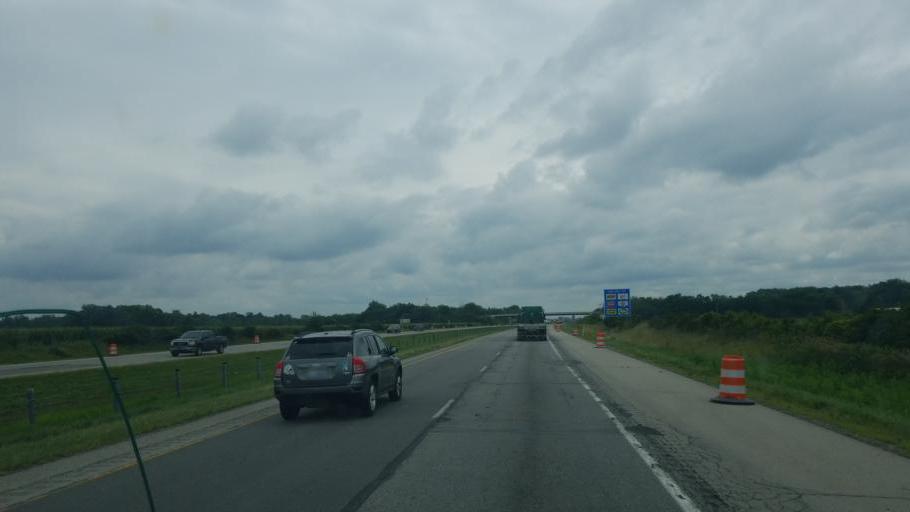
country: US
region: Indiana
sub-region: Madison County
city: Anderson
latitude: 40.0486
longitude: -85.6825
